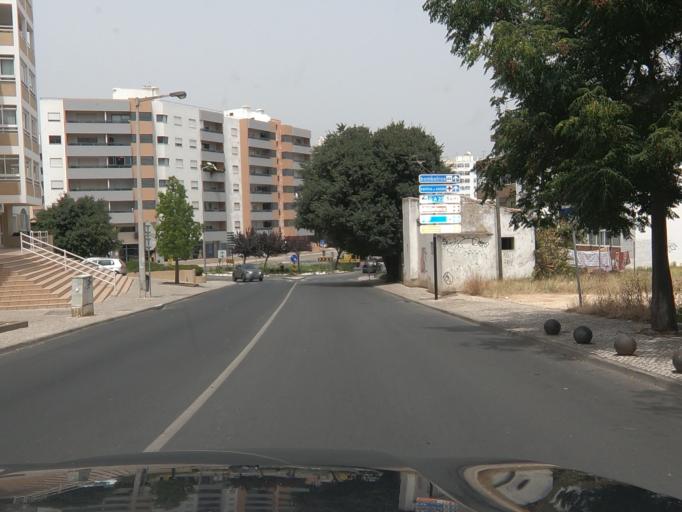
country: PT
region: Faro
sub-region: Portimao
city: Portimao
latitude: 37.1326
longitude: -8.5422
